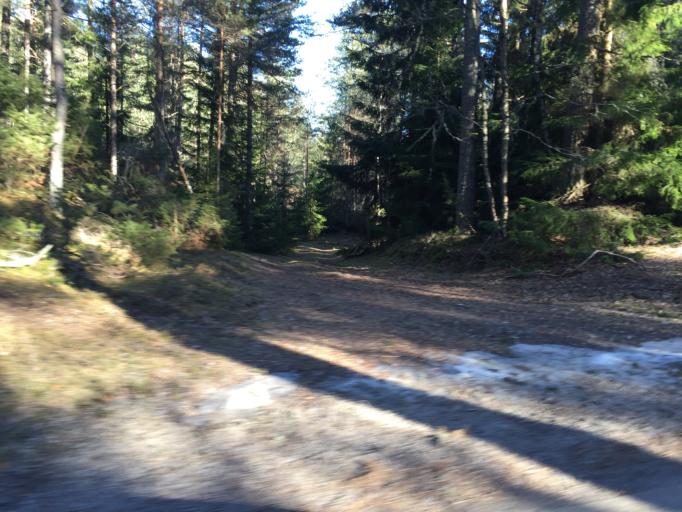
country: SE
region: Soedermanland
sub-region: Vingakers Kommun
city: Vingaker
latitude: 58.9525
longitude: 15.6643
